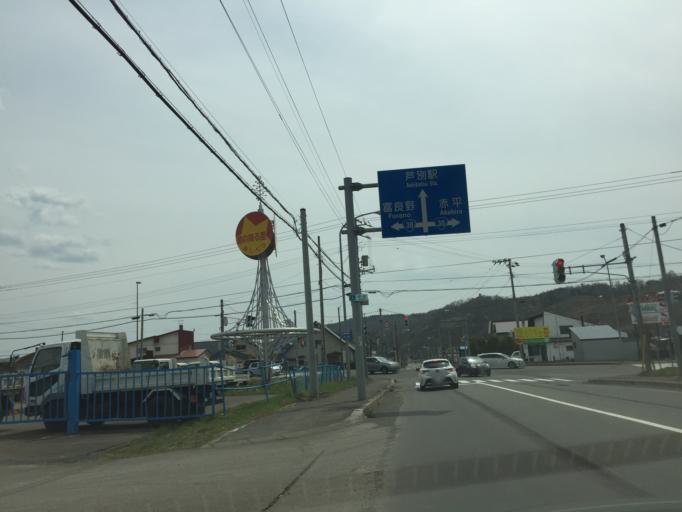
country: JP
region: Hokkaido
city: Ashibetsu
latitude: 43.5313
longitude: 142.1706
